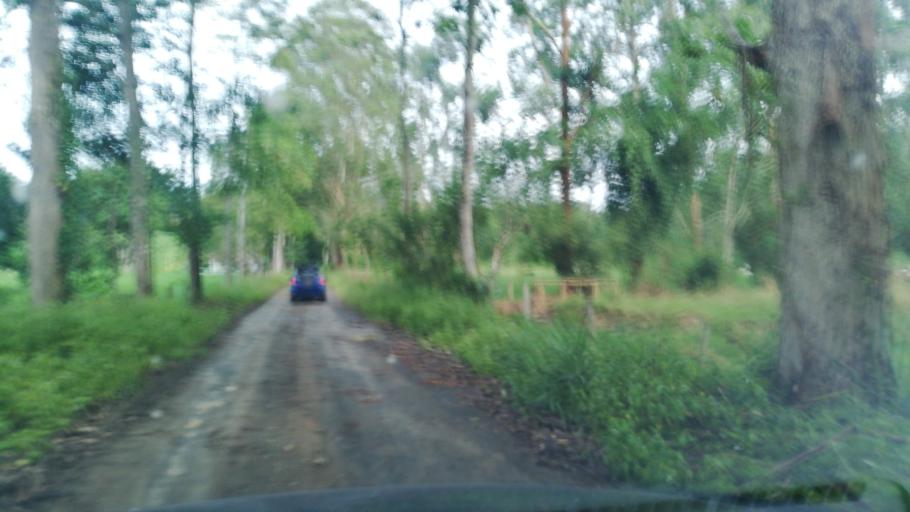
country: CO
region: Valle del Cauca
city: Restrepo
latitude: 3.8532
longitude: -76.4633
